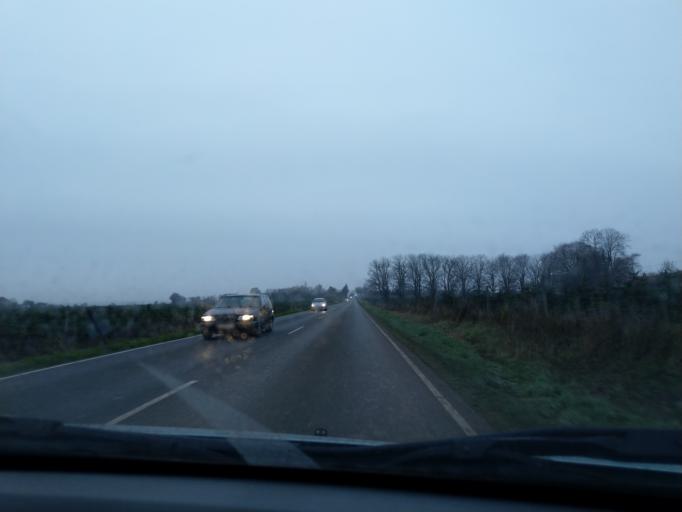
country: DK
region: Zealand
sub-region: Vordingborg Kommune
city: Orslev
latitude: 55.1194
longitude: 11.9794
